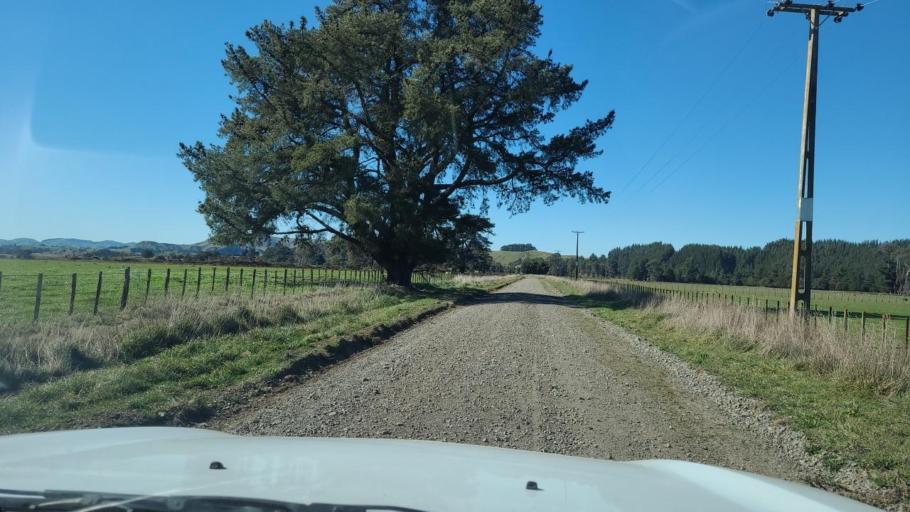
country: NZ
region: Hawke's Bay
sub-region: Napier City
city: Taradale
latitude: -39.4638
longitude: 176.5941
